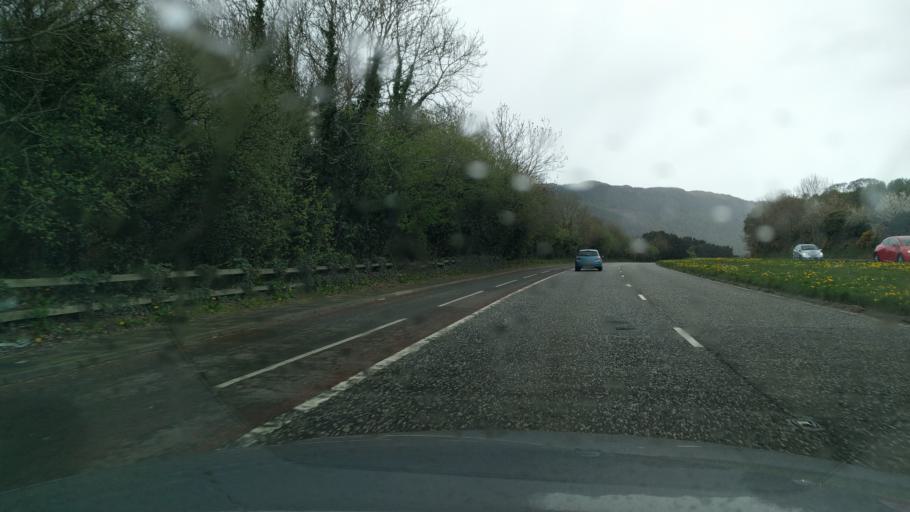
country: GB
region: Northern Ireland
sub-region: Down District
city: Warrenpoint
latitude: 54.1131
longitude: -6.2866
